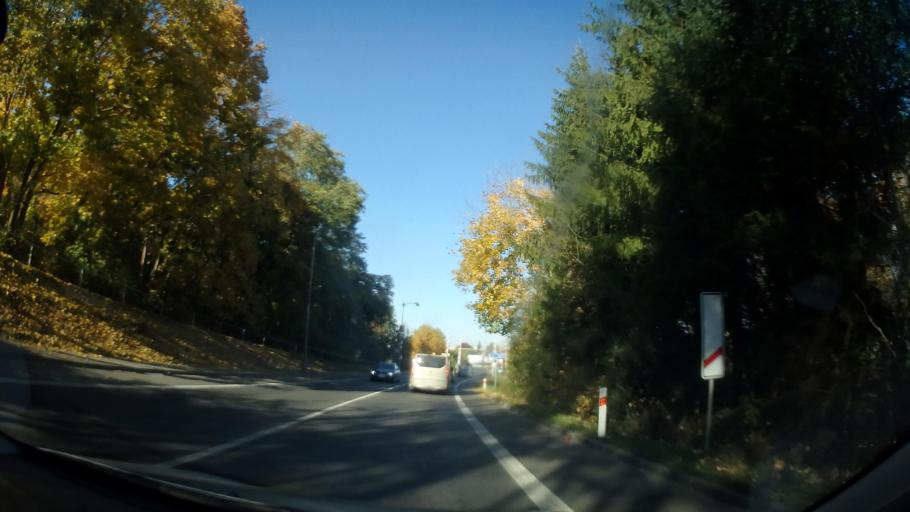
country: CZ
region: Pardubicky
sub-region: Okres Chrudim
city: Chrudim
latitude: 49.9392
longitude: 15.7947
